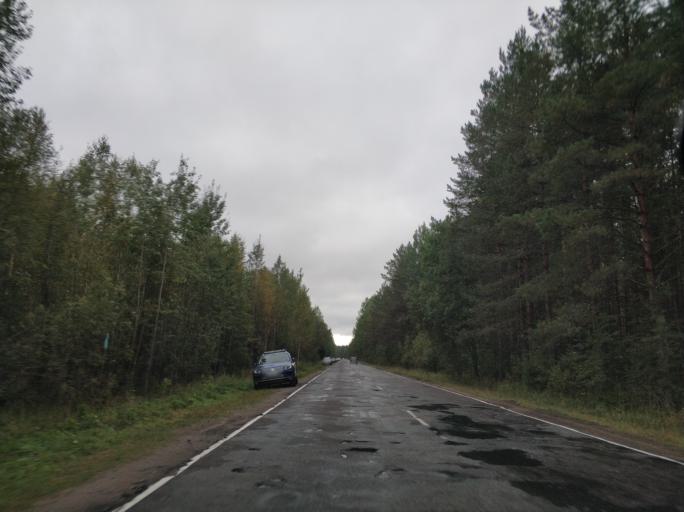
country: RU
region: Leningrad
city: Borisova Griva
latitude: 60.1712
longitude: 30.9199
